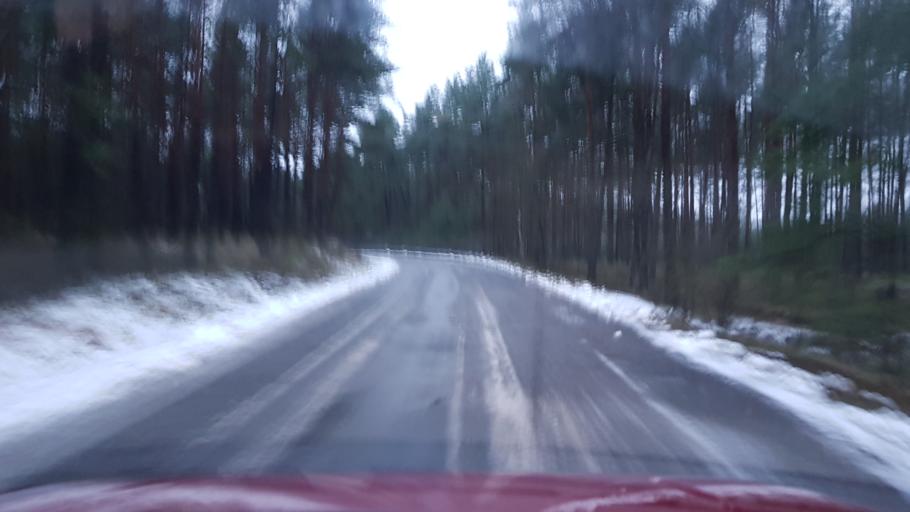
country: PL
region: West Pomeranian Voivodeship
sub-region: Powiat goleniowski
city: Goleniow
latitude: 53.4751
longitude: 14.8336
